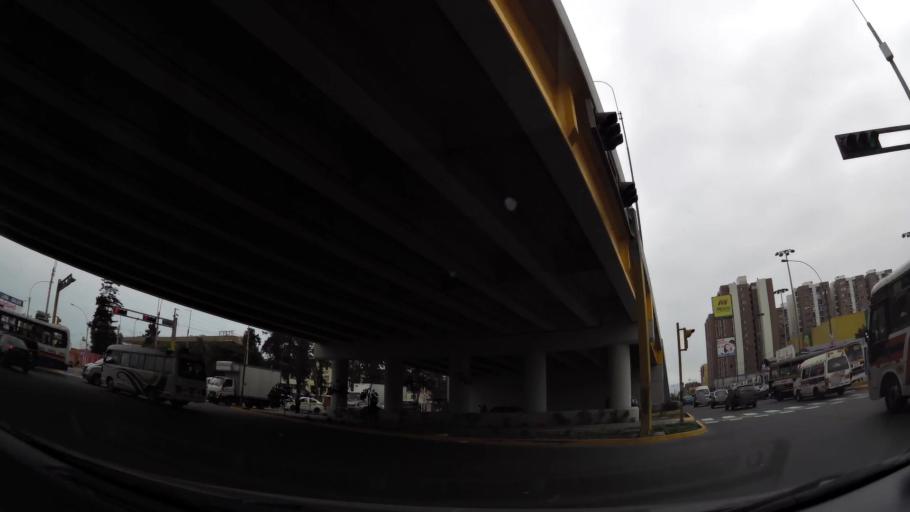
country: PE
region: Callao
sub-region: Callao
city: Callao
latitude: -12.0499
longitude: -77.0783
